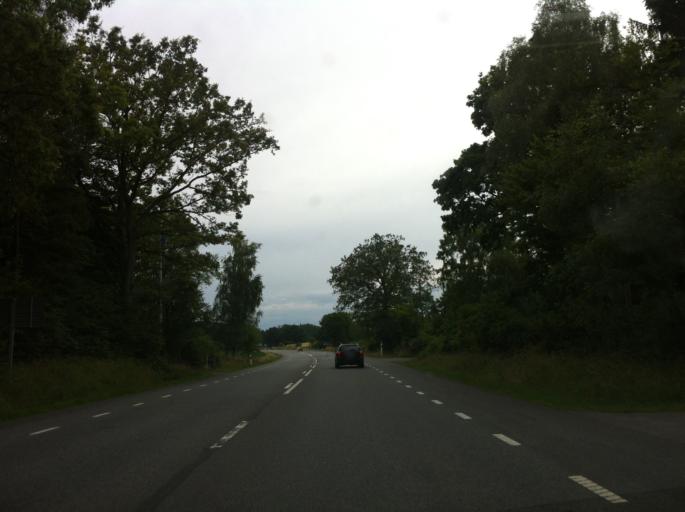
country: SE
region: Skane
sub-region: Hassleholms Kommun
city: Tormestorp
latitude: 56.0775
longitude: 13.7481
